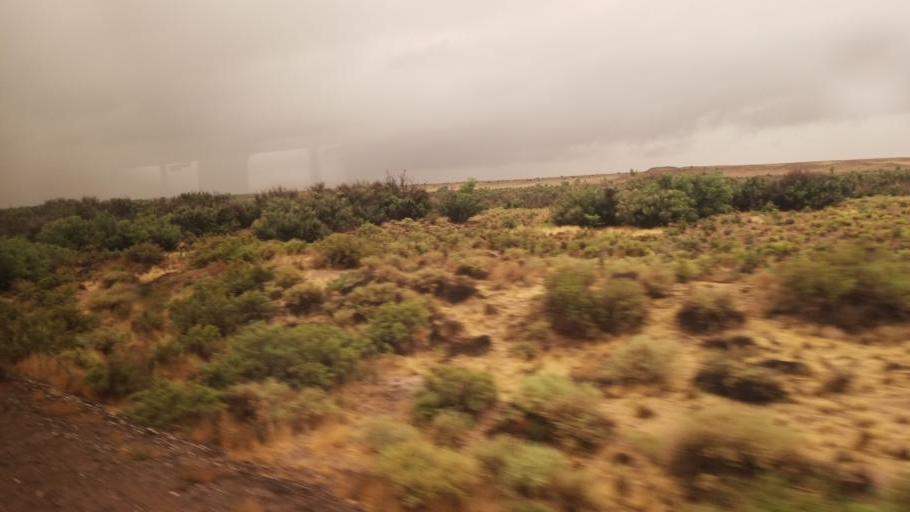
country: US
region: Arizona
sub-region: Navajo County
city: Joseph City
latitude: 34.9622
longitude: -110.3977
